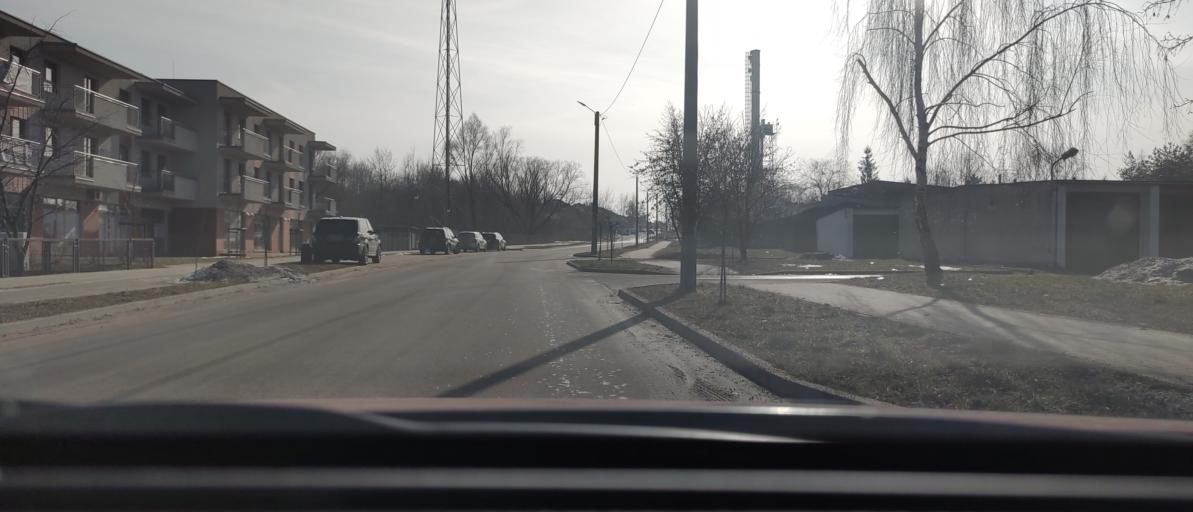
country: PL
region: Masovian Voivodeship
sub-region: Powiat bialobrzeski
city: Bialobrzegi
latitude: 51.6422
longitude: 20.9515
